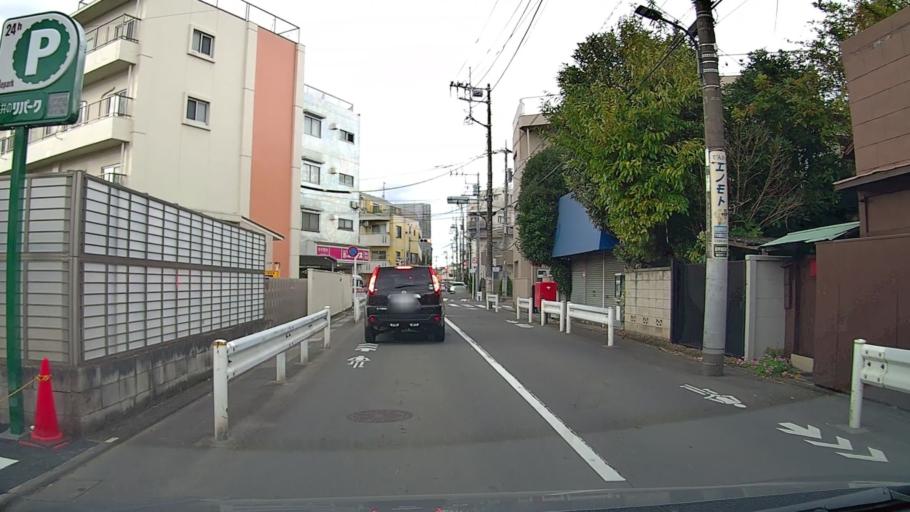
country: JP
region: Saitama
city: Wako
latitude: 35.7298
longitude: 139.6158
